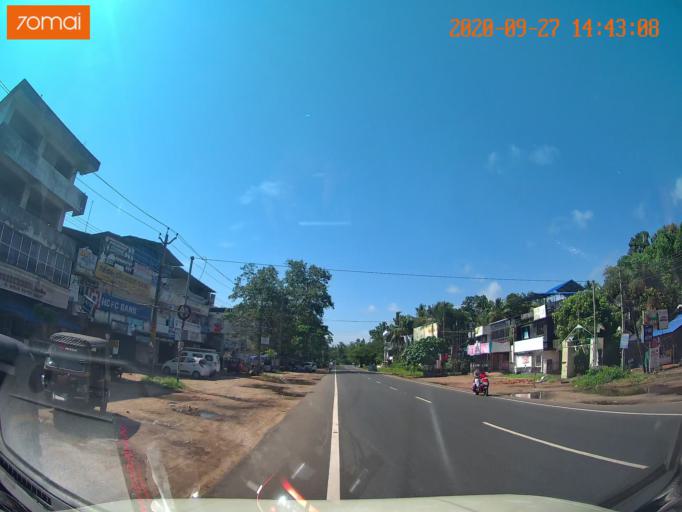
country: IN
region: Kerala
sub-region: Thrissur District
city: Thanniyam
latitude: 10.4410
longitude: 76.0943
